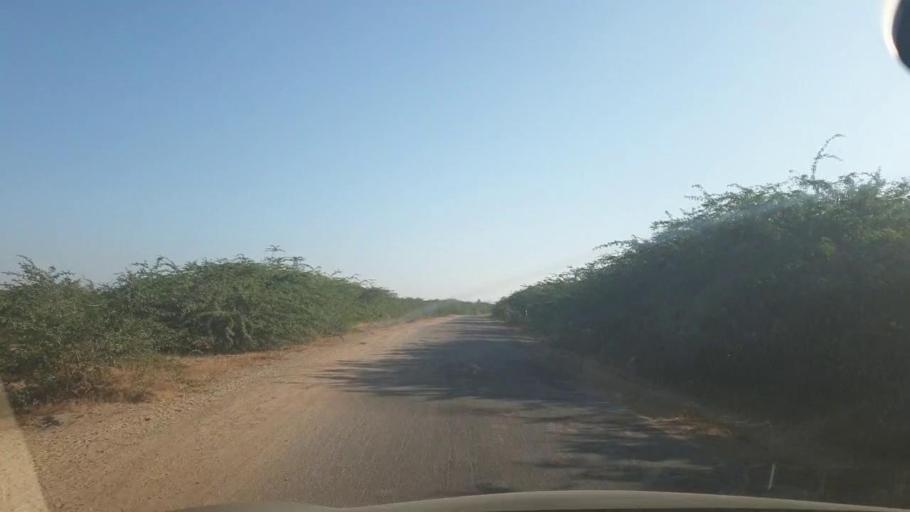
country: PK
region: Sindh
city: Malir Cantonment
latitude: 25.1133
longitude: 67.2699
